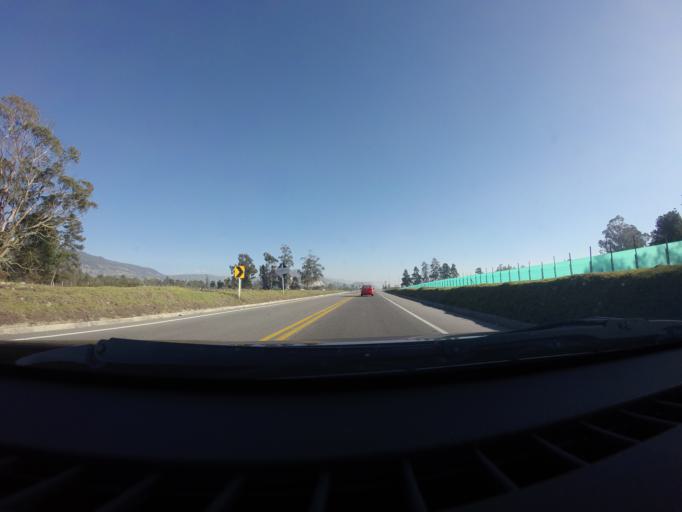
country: CO
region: Cundinamarca
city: Cogua
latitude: 5.0398
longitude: -73.9705
